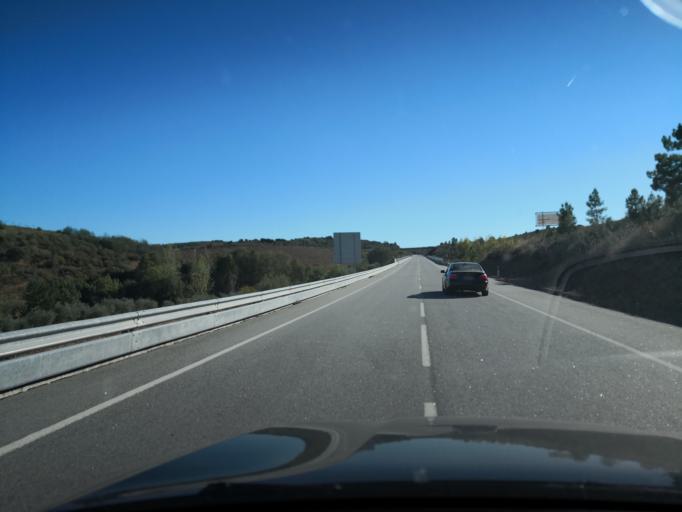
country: PT
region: Braganca
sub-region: Mirandela
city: Mirandela
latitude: 41.5122
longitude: -7.2274
